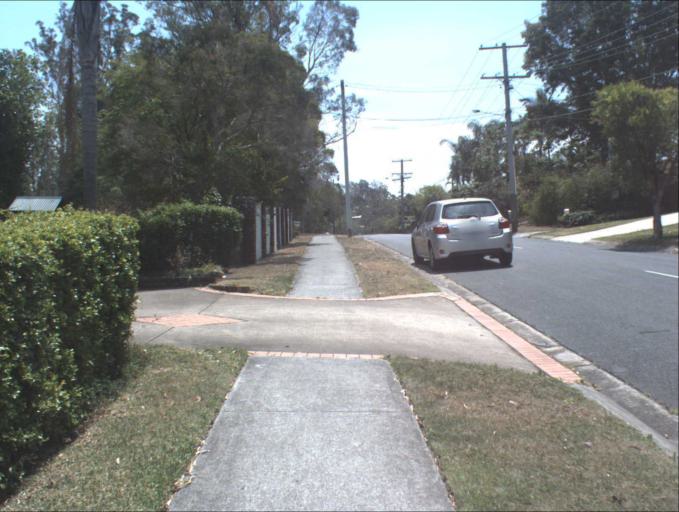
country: AU
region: Queensland
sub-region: Logan
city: Beenleigh
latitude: -27.6686
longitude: 153.1936
